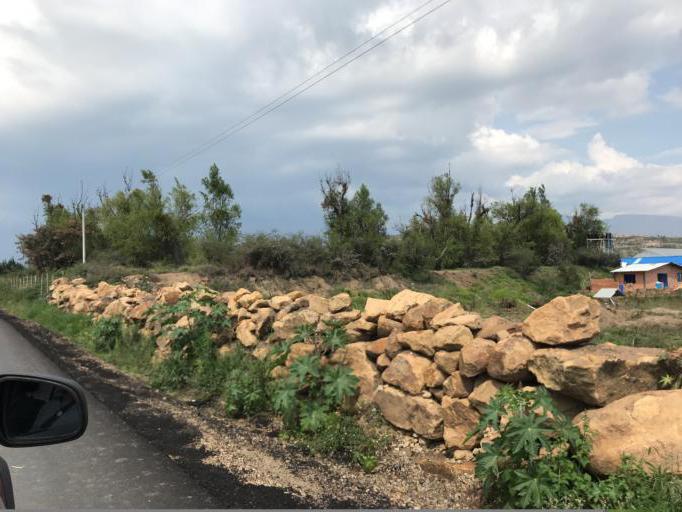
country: CO
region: Boyaca
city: Sutamarchan
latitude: 5.6368
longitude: -73.5992
